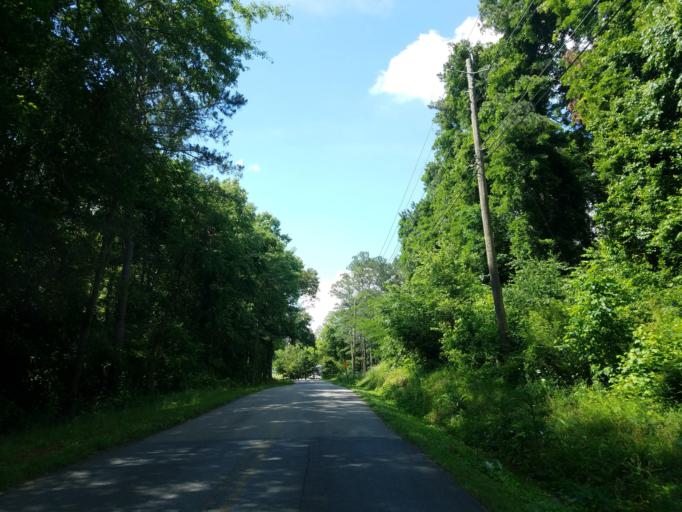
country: US
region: Georgia
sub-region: Cherokee County
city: Holly Springs
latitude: 34.1611
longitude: -84.5137
